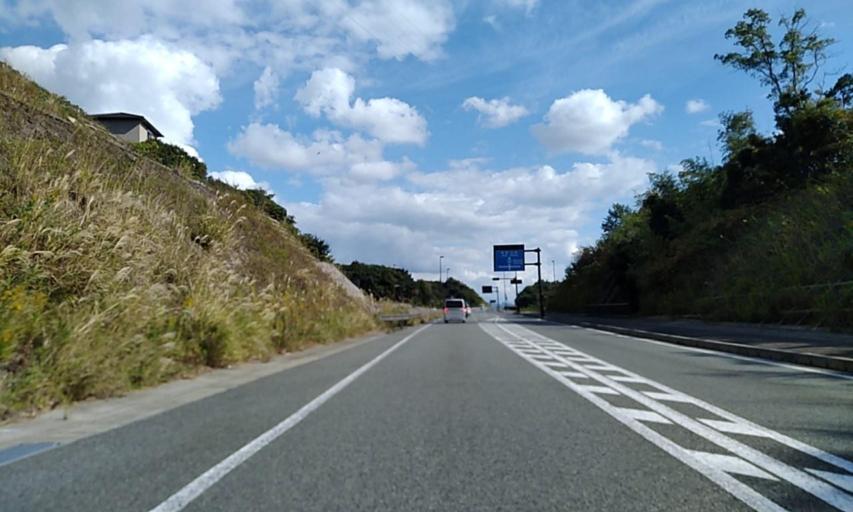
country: JP
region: Wakayama
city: Tanabe
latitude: 33.7497
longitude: 135.3596
